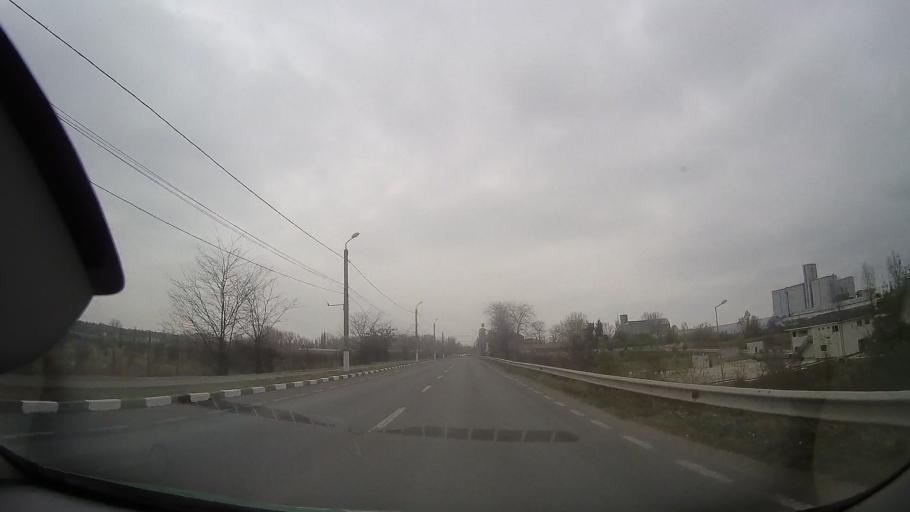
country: RO
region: Ialomita
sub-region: Comuna Manasia
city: Manasia
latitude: 44.7112
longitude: 26.6616
